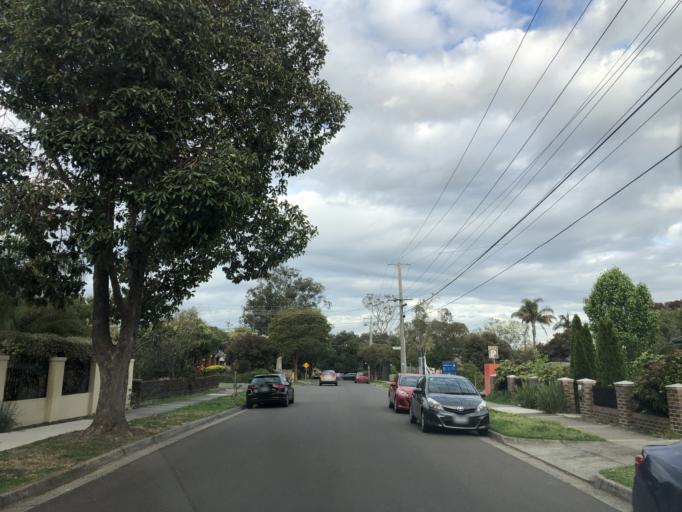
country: AU
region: Victoria
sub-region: Whitehorse
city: Burwood
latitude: -37.8636
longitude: 145.1229
